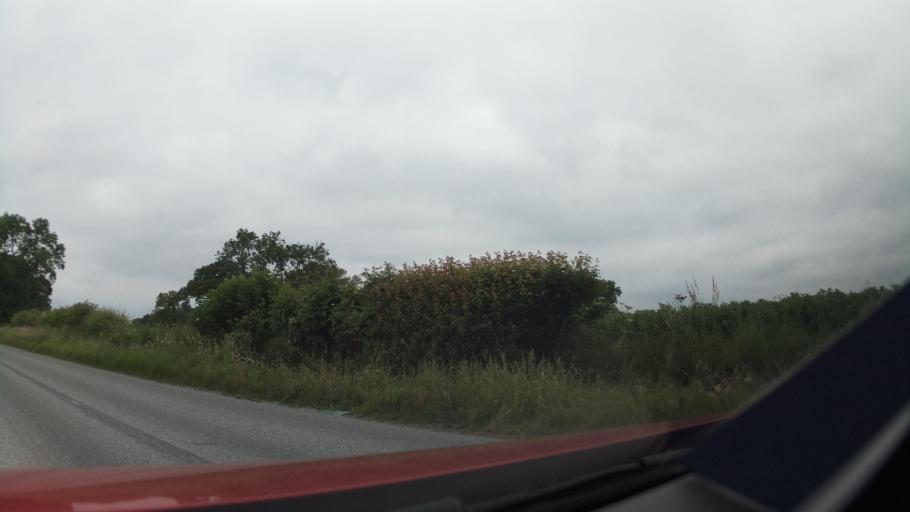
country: GB
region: England
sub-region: District of Rutland
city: Exton
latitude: 52.6725
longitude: -0.6511
